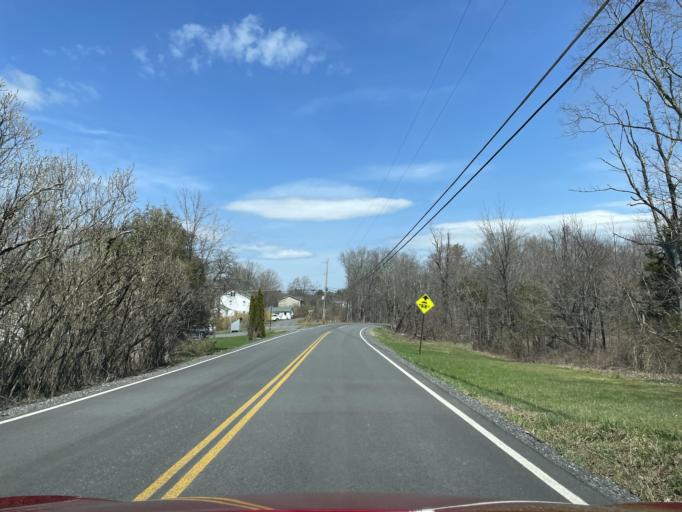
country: US
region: New York
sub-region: Ulster County
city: Manorville
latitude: 42.1399
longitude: -74.0083
